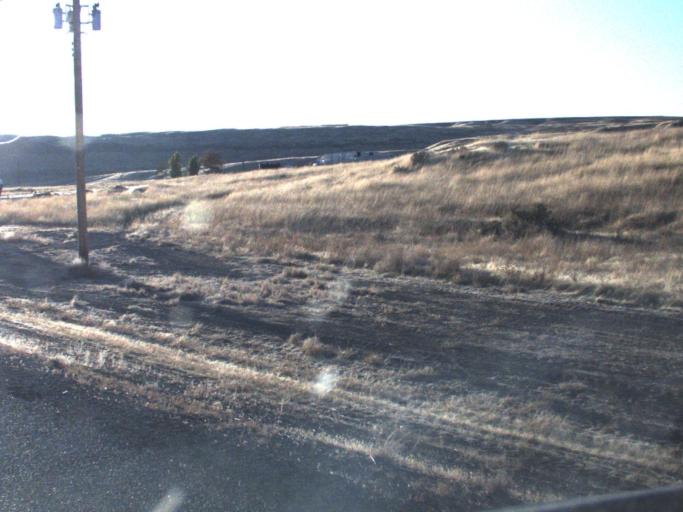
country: US
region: Washington
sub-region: Franklin County
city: Connell
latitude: 46.6634
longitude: -118.4855
